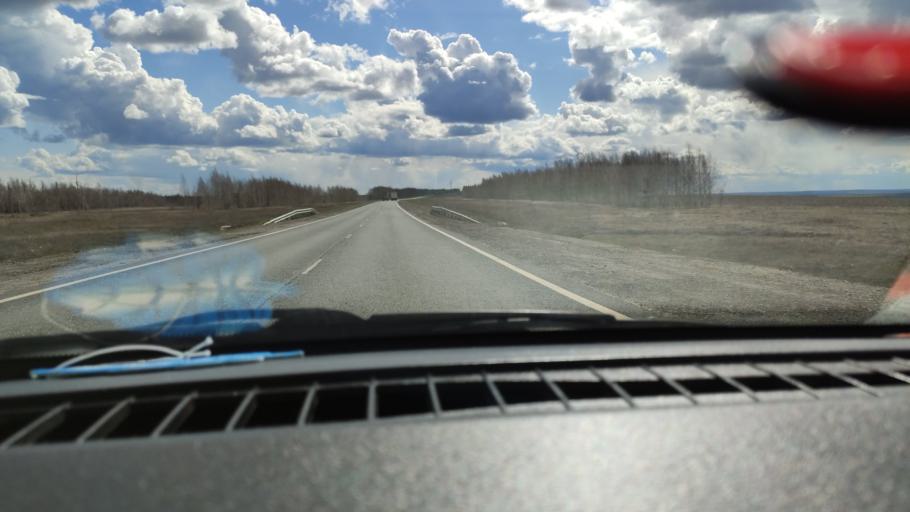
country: RU
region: Saratov
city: Dukhovnitskoye
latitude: 52.8496
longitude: 48.2558
